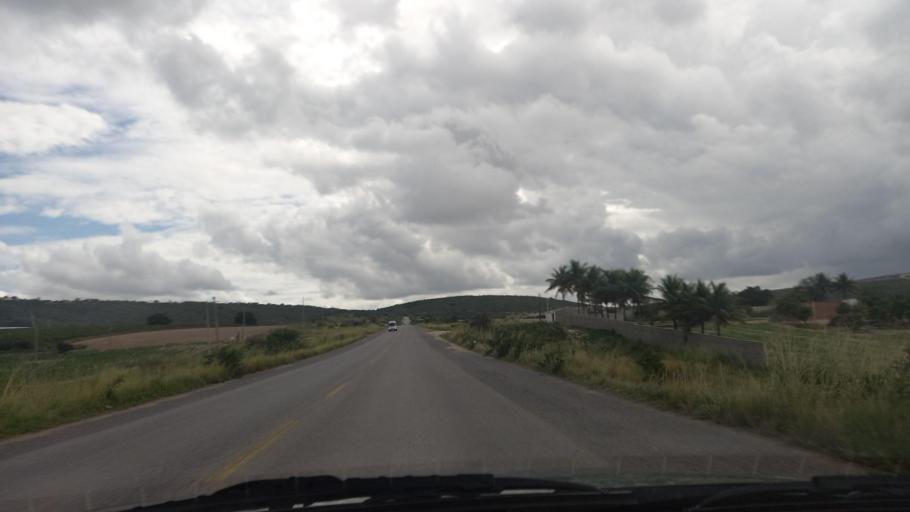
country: BR
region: Pernambuco
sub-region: Lajedo
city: Lajedo
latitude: -8.6707
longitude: -36.3850
